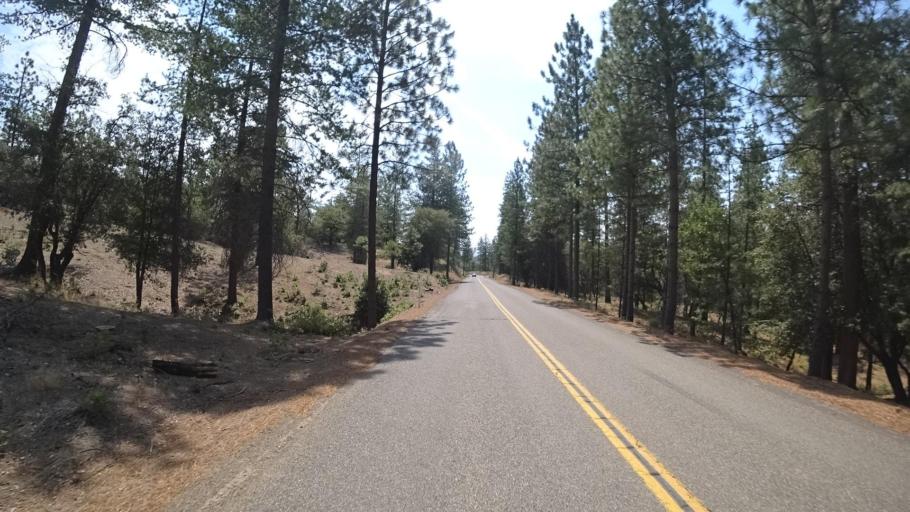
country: US
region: California
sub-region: Tuolumne County
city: Tuolumne City
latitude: 37.7290
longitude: -120.1149
